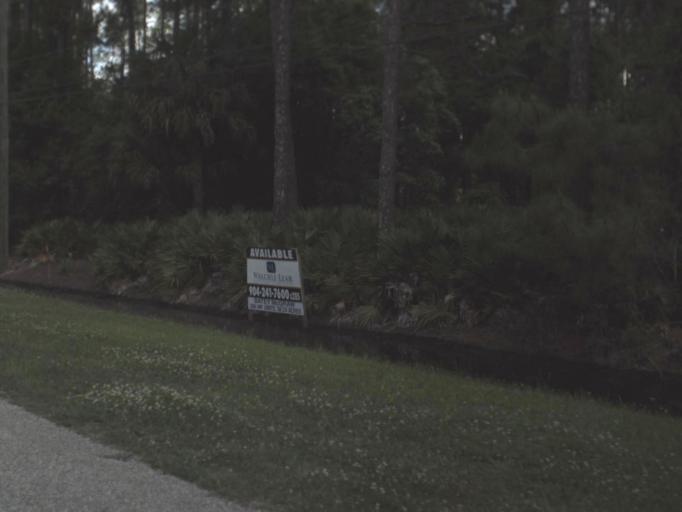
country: US
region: Florida
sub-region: Saint Johns County
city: Palm Valley
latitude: 30.1110
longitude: -81.4852
